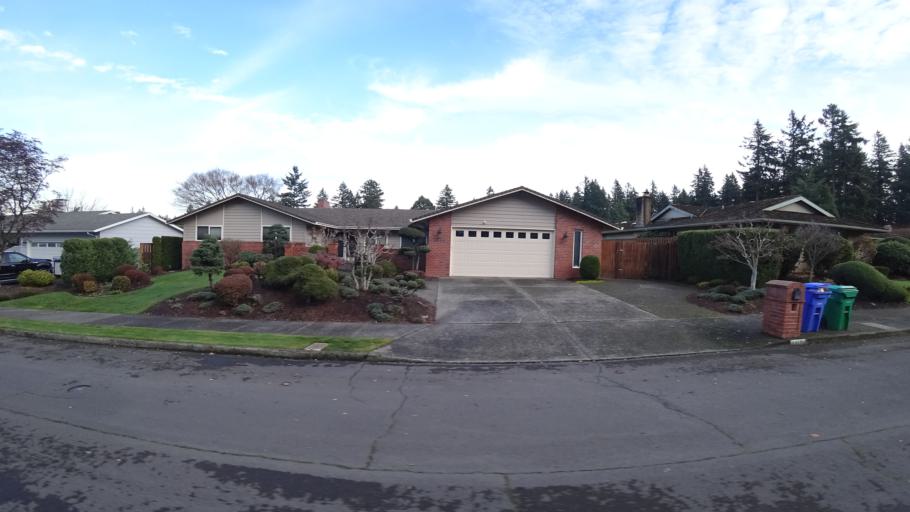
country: US
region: Oregon
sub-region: Multnomah County
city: Lents
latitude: 45.5308
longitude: -122.5243
